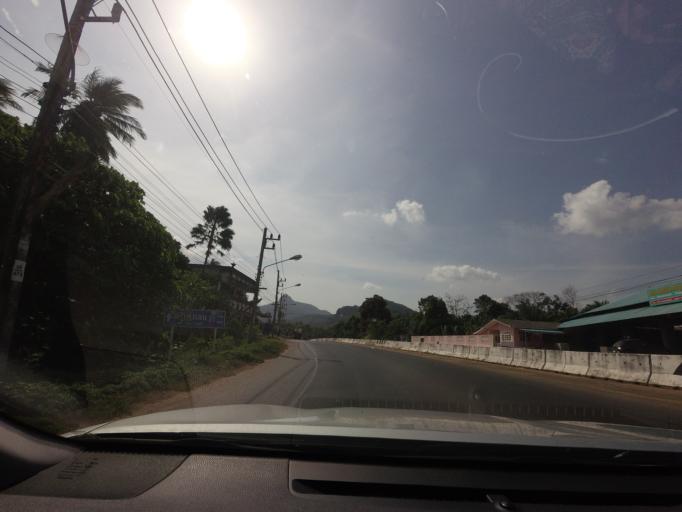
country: TH
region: Phangnga
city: Ban Ao Nang
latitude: 8.0941
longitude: 98.8100
